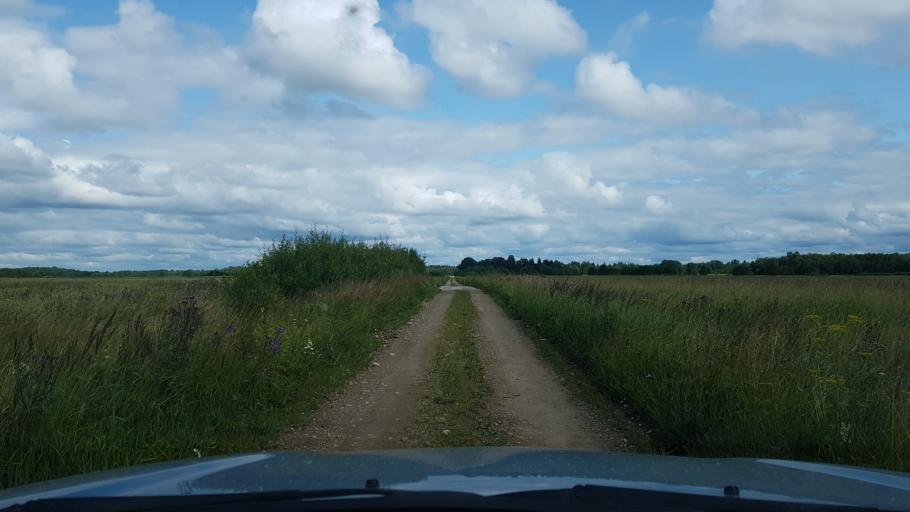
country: EE
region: Ida-Virumaa
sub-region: Narva-Joesuu linn
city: Narva-Joesuu
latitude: 59.3701
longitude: 27.9347
